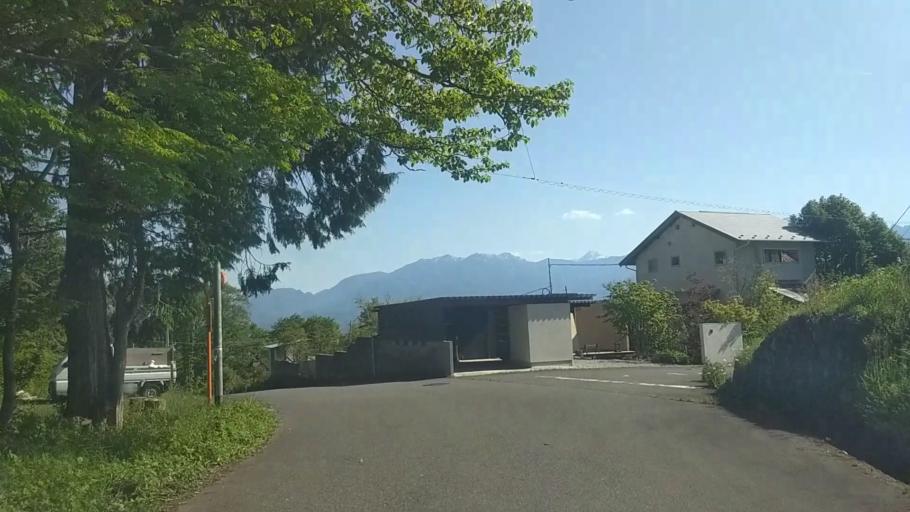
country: JP
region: Yamanashi
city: Nirasaki
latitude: 35.8759
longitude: 138.3604
